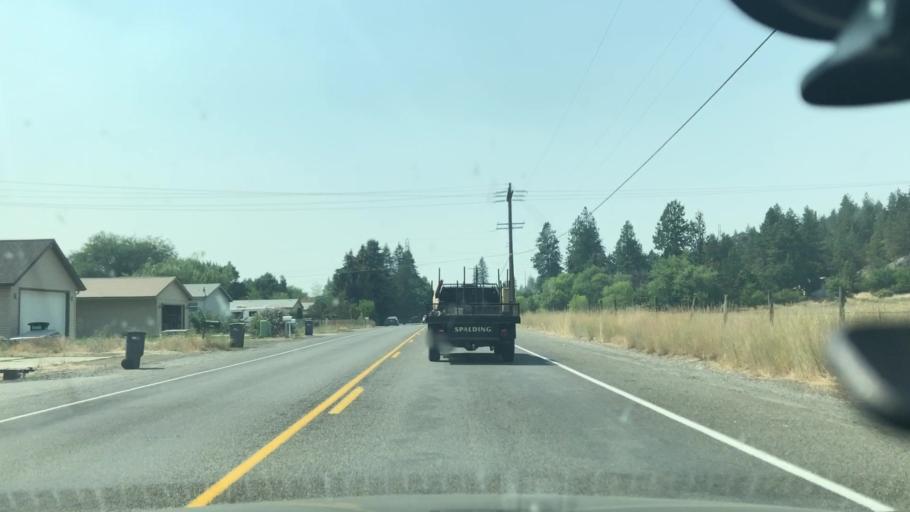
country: US
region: Washington
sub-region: Spokane County
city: Millwood
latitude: 47.6856
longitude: -117.3349
